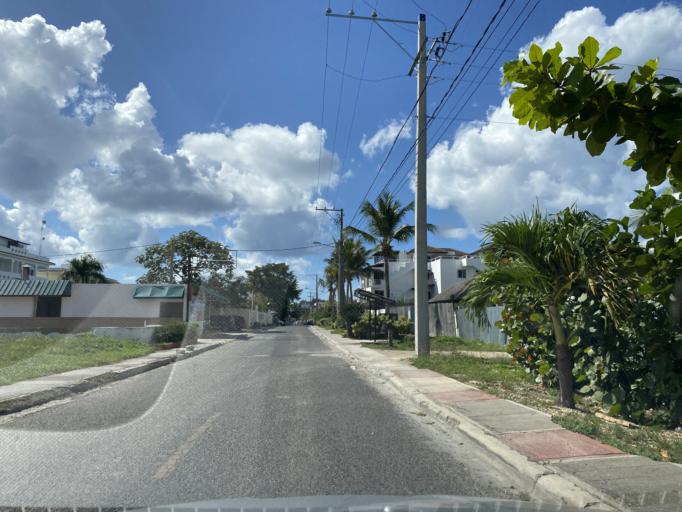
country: DO
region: La Romana
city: La Romana
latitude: 18.3520
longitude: -68.8270
